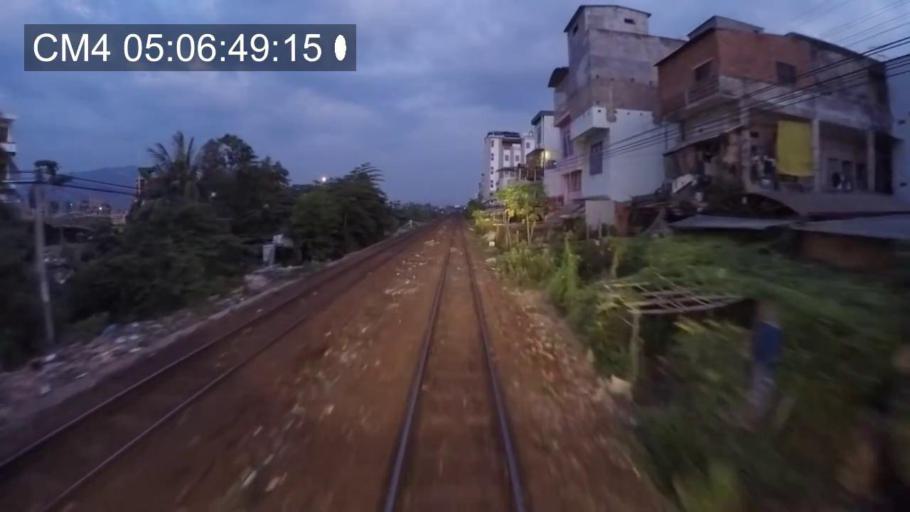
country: VN
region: Khanh Hoa
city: Nha Trang
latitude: 12.2806
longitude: 109.1817
